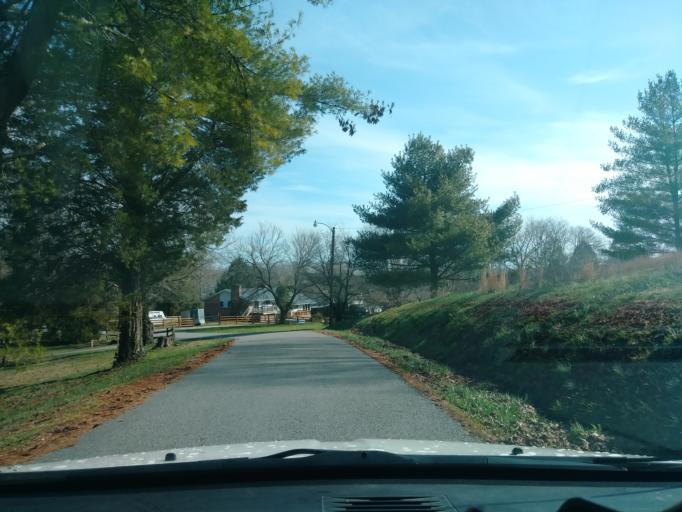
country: US
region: Tennessee
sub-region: Campbell County
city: Hunter
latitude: 36.3632
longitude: -84.1282
